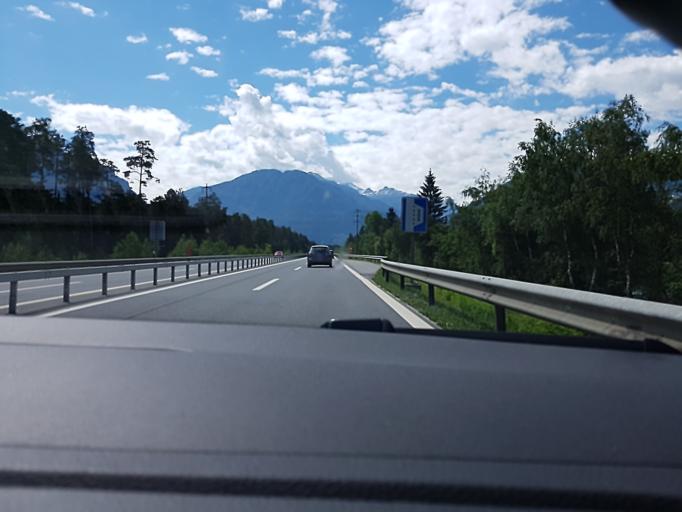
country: CH
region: Grisons
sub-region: Hinterrhein District
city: Cazis
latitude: 46.7506
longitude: 9.4289
